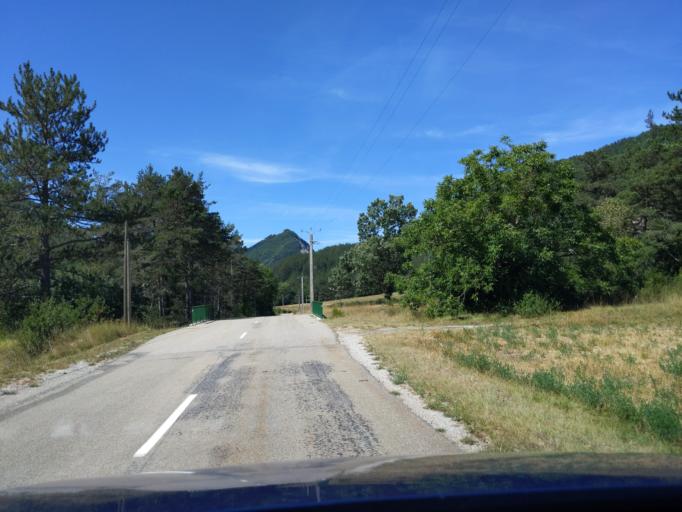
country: FR
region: Rhone-Alpes
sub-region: Departement de la Drome
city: Die
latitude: 44.6171
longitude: 5.5021
